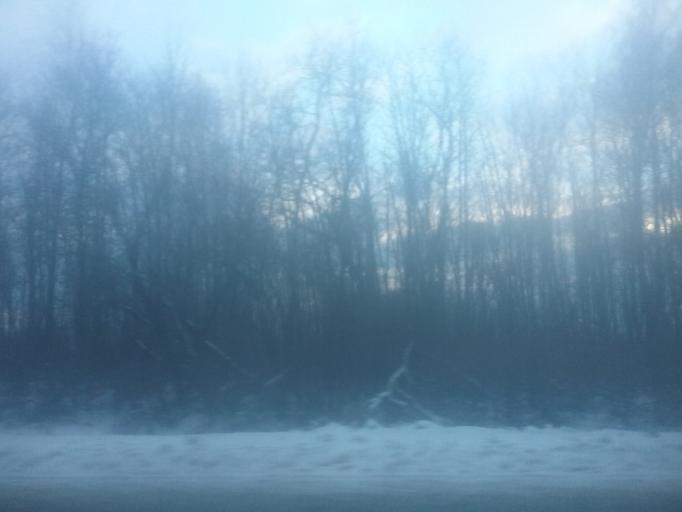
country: RU
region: Tula
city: Shvartsevskiy
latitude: 54.0253
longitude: 37.9620
